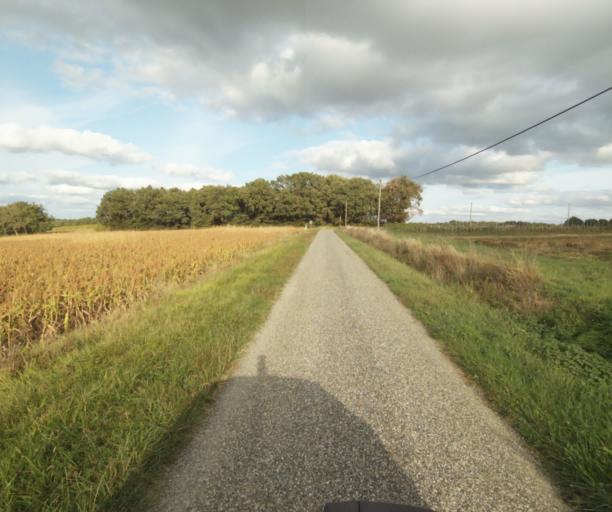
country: FR
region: Midi-Pyrenees
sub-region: Departement de la Haute-Garonne
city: Launac
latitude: 43.8222
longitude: 1.1006
